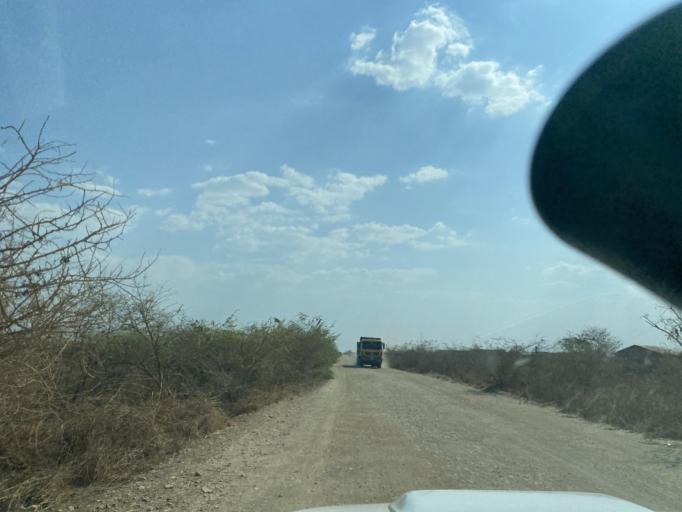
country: ZM
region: Lusaka
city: Lusaka
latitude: -15.3615
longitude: 28.0925
